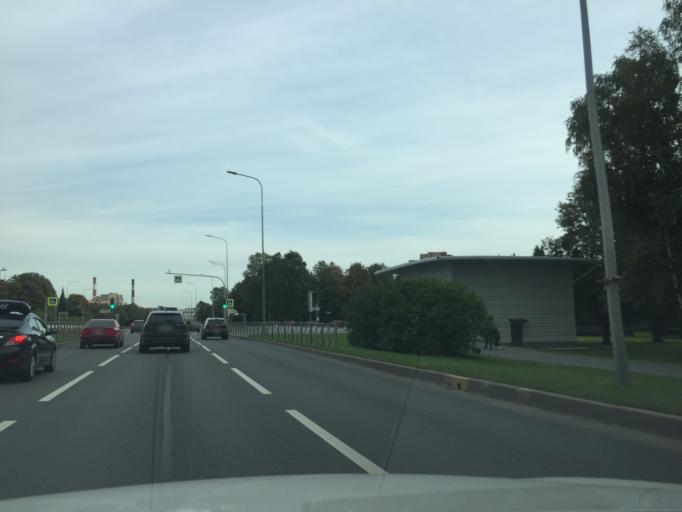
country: RU
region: Leningrad
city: Kalininskiy
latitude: 59.9941
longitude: 30.4181
